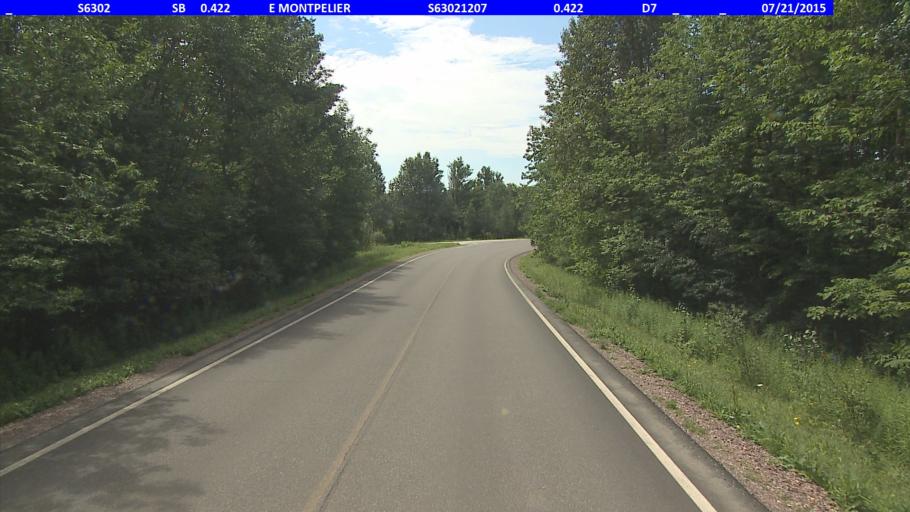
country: US
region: Vermont
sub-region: Washington County
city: Montpelier
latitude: 44.2494
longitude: -72.5215
